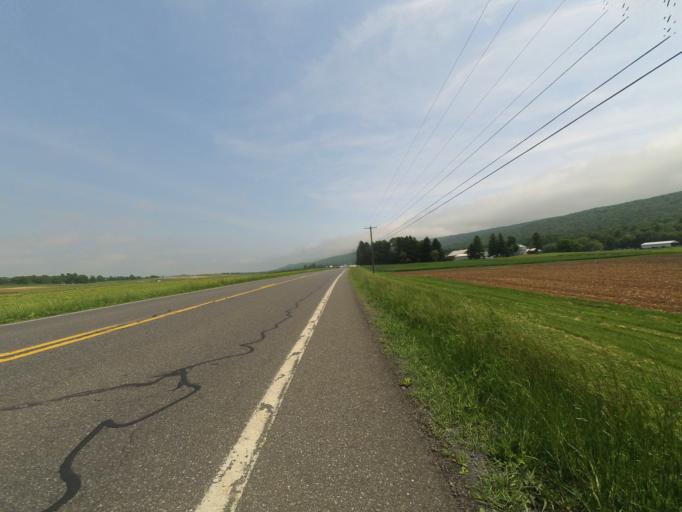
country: US
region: Pennsylvania
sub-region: Centre County
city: Pine Grove Mills
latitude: 40.7168
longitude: -77.9377
